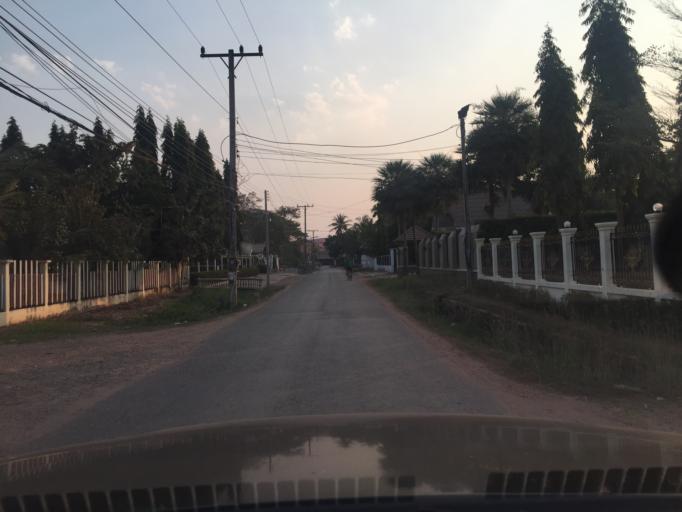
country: LA
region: Vientiane
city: Vientiane
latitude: 17.9810
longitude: 102.5882
